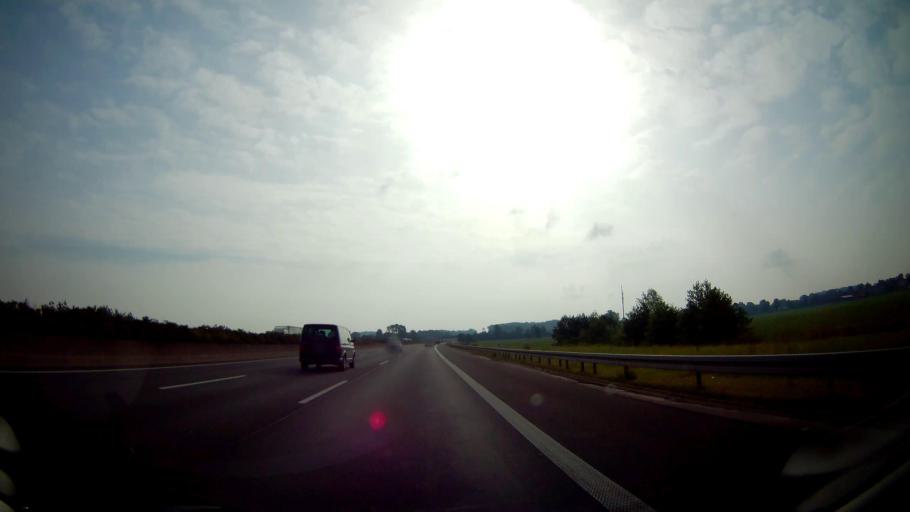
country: DE
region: North Rhine-Westphalia
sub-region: Regierungsbezirk Arnsberg
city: Bonen
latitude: 51.6222
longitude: 7.8123
